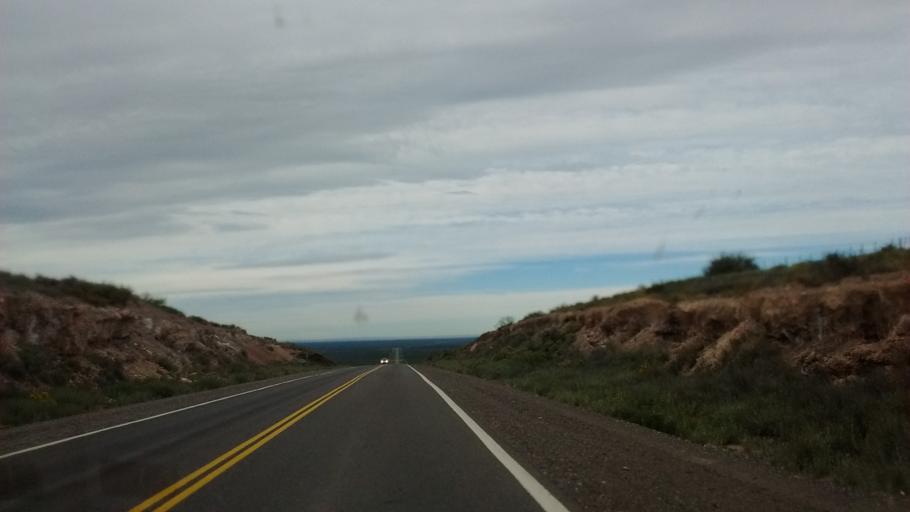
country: AR
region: Rio Negro
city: Contraalmirante Cordero
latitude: -38.4005
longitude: -68.0299
